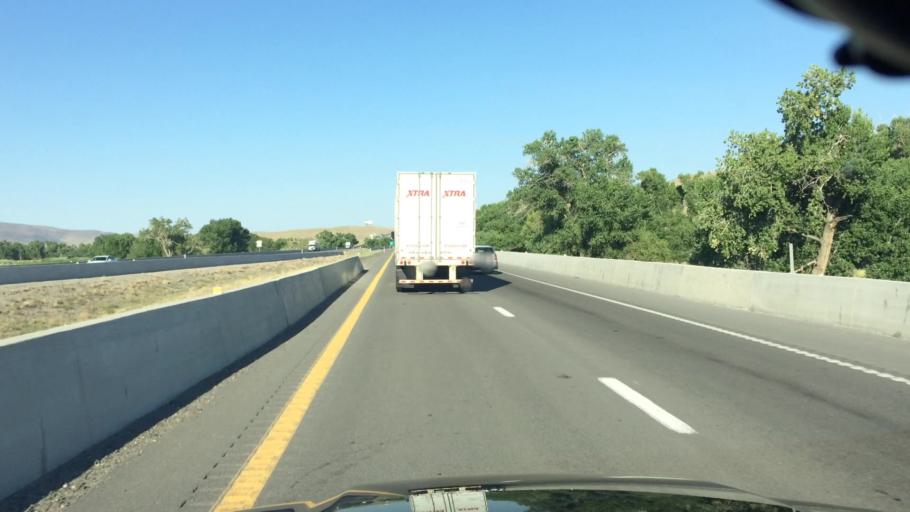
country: US
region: Nevada
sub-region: Lyon County
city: Fernley
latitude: 39.6171
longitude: -119.3010
